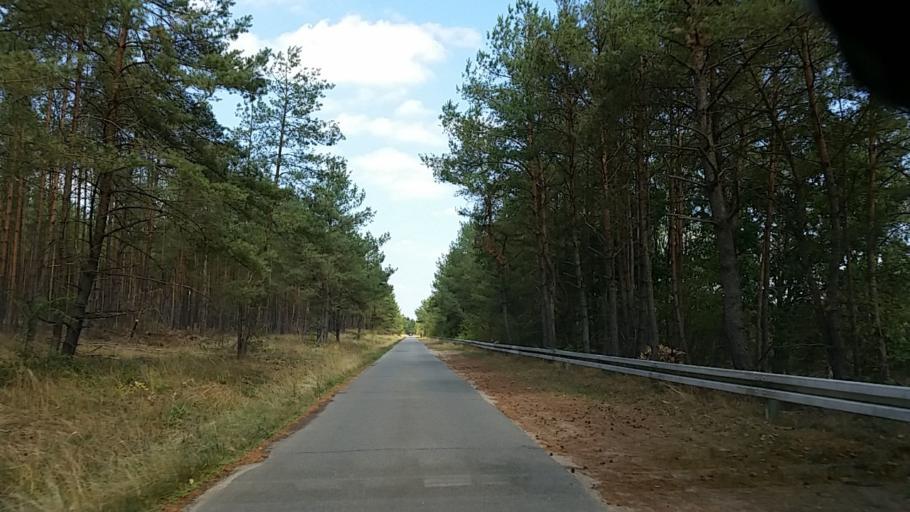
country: DE
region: Lower Saxony
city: Wendisch Evern
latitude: 53.2296
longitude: 10.4892
